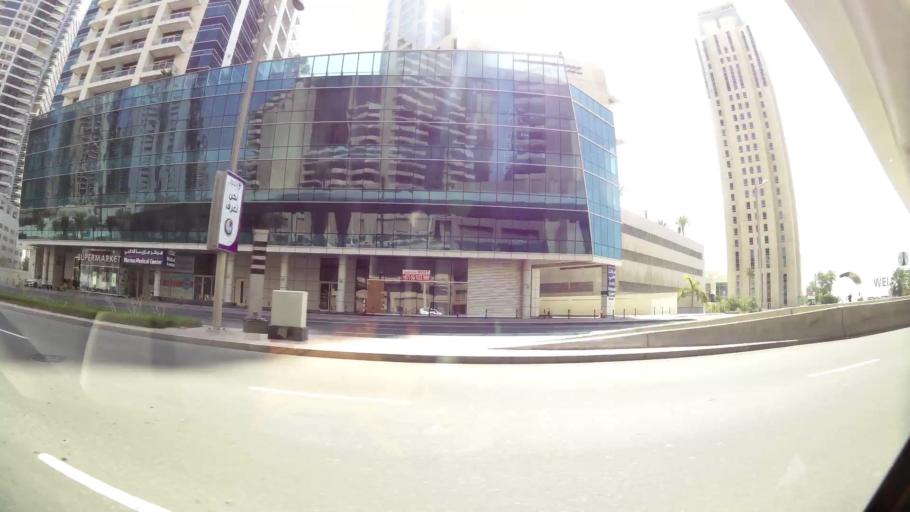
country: AE
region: Dubai
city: Dubai
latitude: 25.0858
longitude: 55.1430
